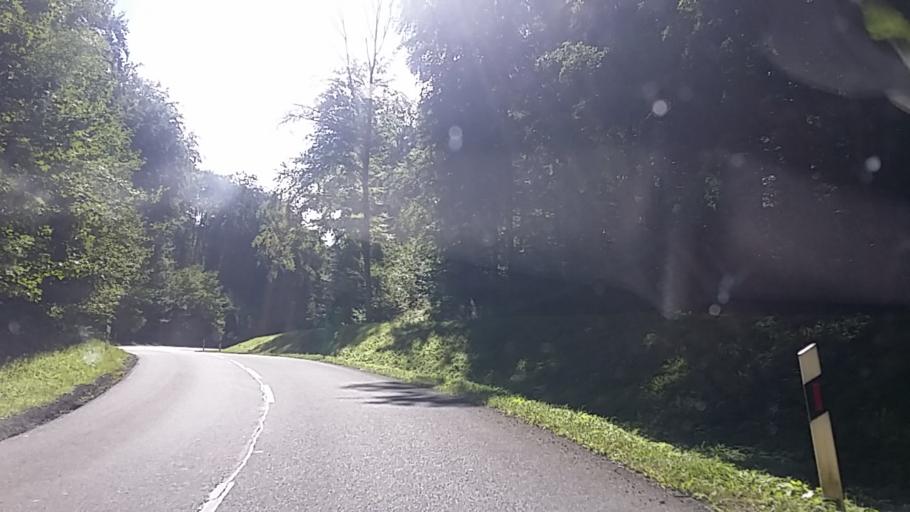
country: HU
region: Baranya
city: Pecs
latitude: 46.1265
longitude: 18.1649
